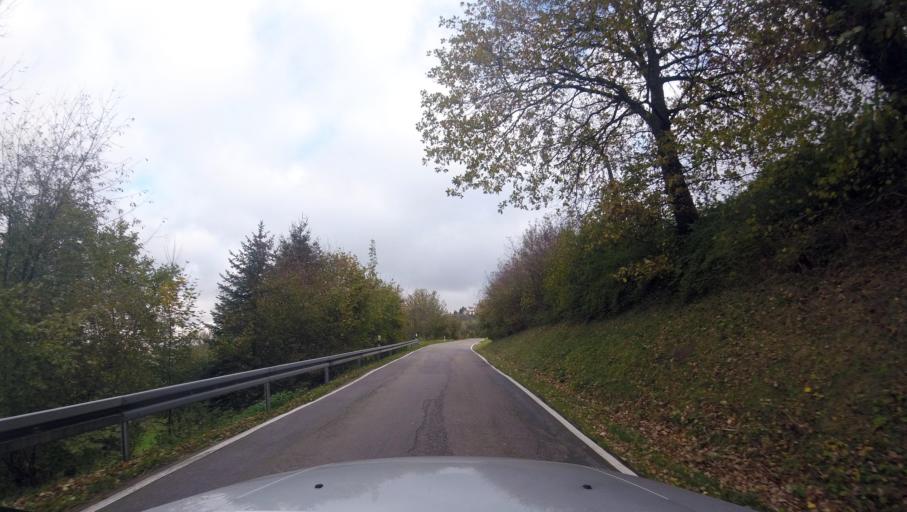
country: DE
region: Baden-Wuerttemberg
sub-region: Regierungsbezirk Stuttgart
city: Winnenden
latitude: 48.8762
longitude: 9.4350
